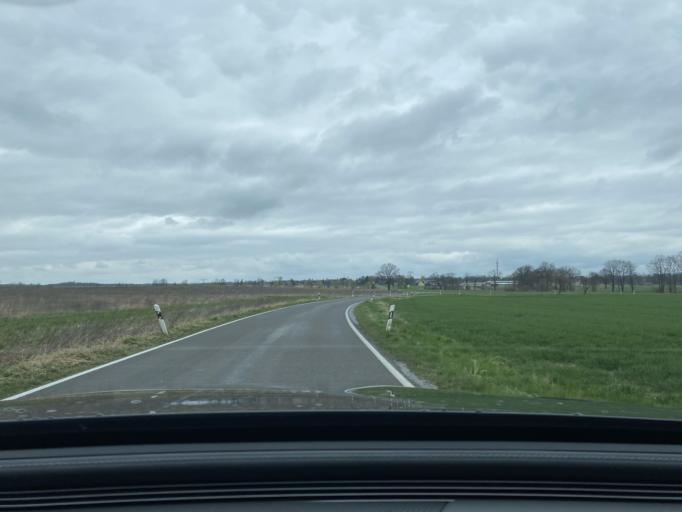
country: DE
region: Saxony
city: Neschwitz
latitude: 51.2565
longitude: 14.3327
